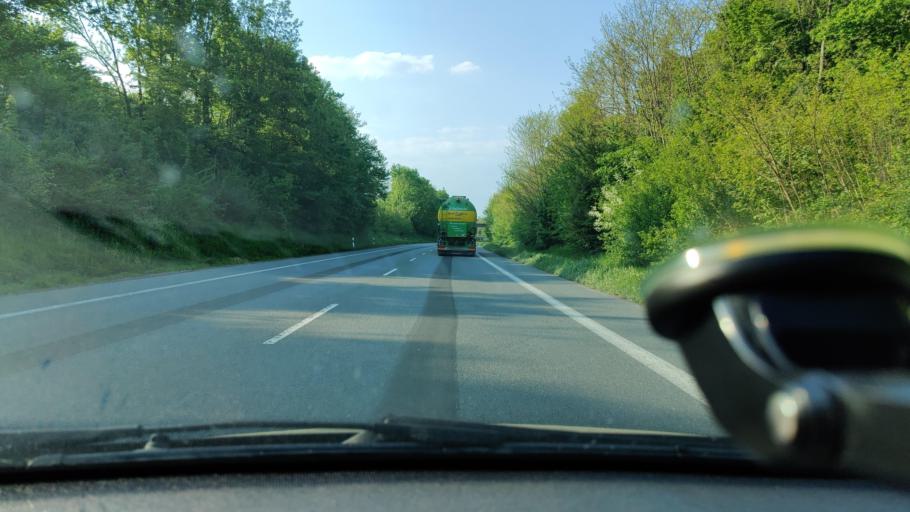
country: DE
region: North Rhine-Westphalia
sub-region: Regierungsbezirk Munster
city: Telgte
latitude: 51.9852
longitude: 7.8100
